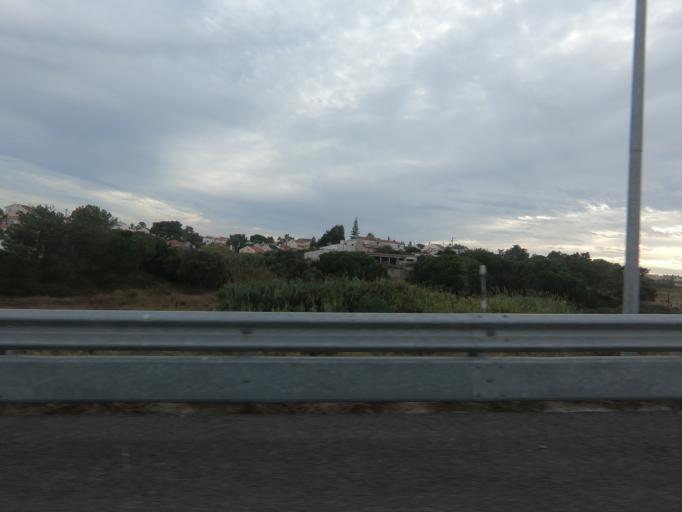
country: PT
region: Setubal
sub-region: Almada
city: Charneca
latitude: 38.6233
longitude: -9.1900
